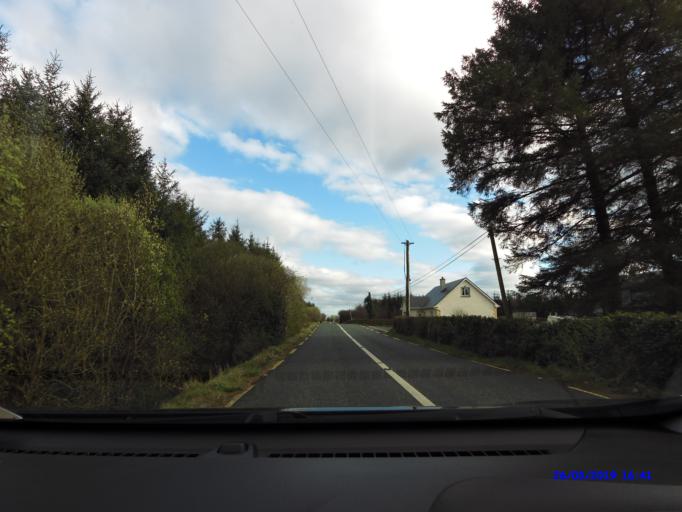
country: IE
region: Connaught
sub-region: Maigh Eo
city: Ballyhaunis
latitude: 53.8713
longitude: -8.7713
